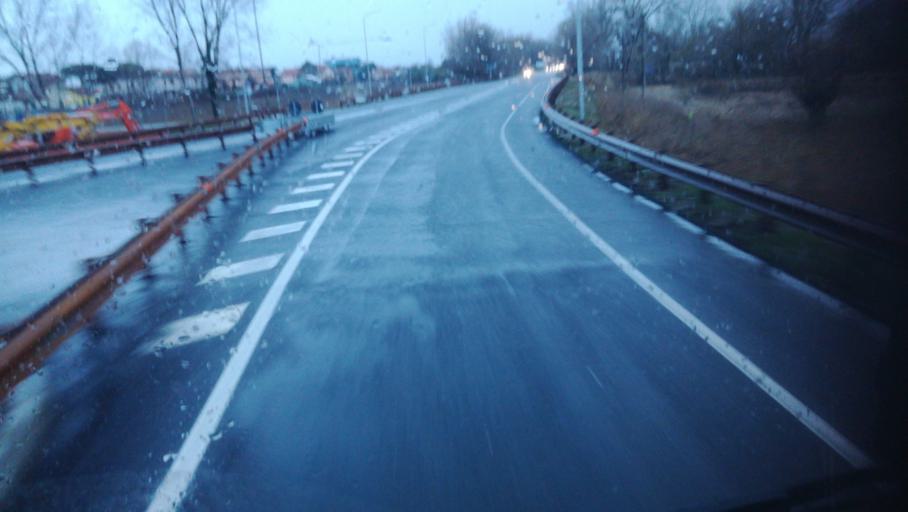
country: IT
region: Emilia-Romagna
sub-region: Provincia di Ravenna
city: Cervia
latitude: 44.2305
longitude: 12.3635
